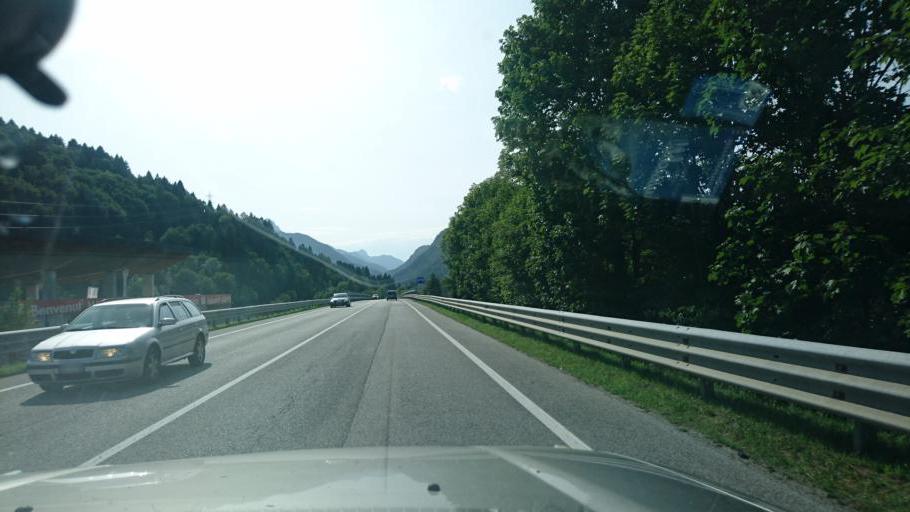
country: IT
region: Friuli Venezia Giulia
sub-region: Provincia di Udine
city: Tarvisio
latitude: 46.5082
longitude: 13.5364
